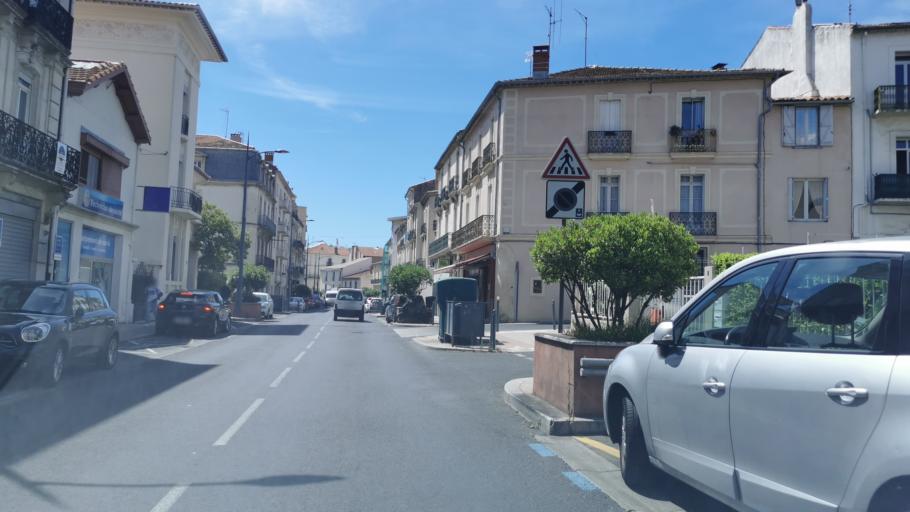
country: FR
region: Languedoc-Roussillon
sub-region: Departement de l'Herault
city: Beziers
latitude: 43.3419
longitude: 3.2217
